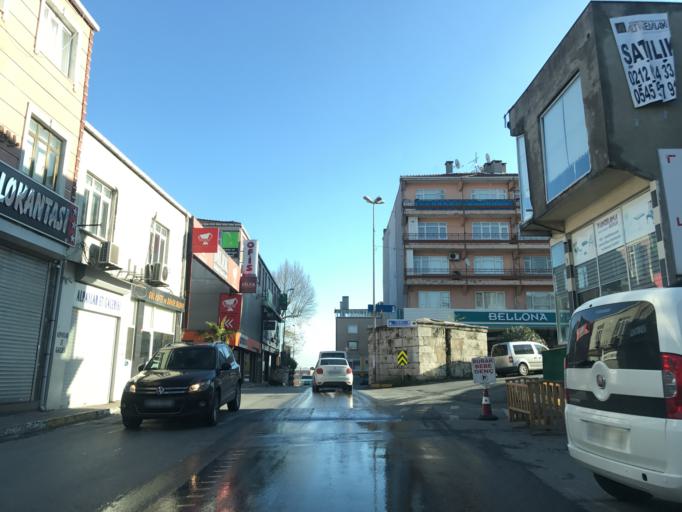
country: TR
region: Istanbul
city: Istanbul
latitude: 41.0382
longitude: 28.9278
